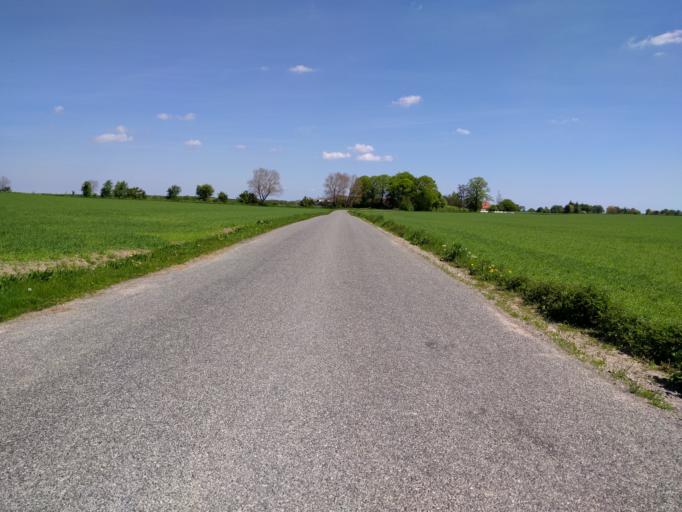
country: DK
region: Zealand
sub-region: Guldborgsund Kommune
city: Nykobing Falster
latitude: 54.7440
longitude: 12.0178
